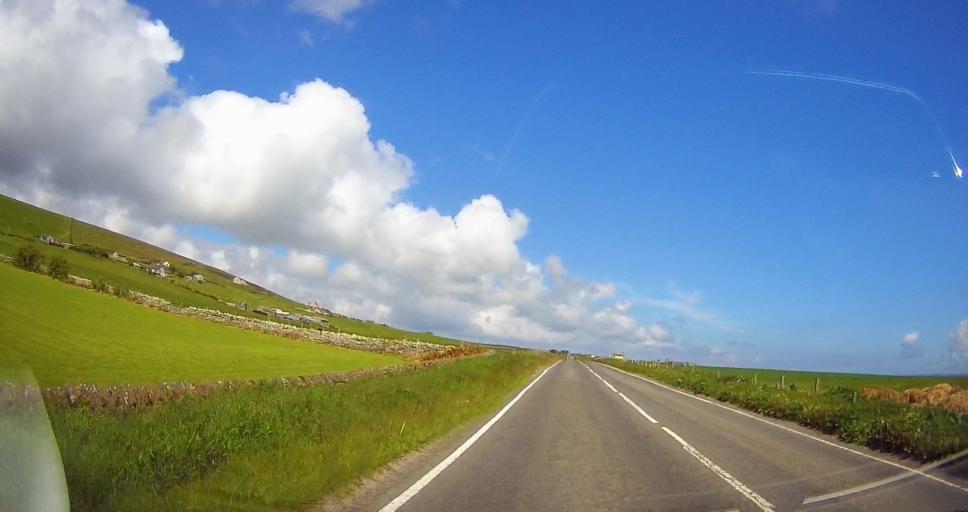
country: GB
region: Scotland
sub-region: Orkney Islands
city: Orkney
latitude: 59.0139
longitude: -3.1091
